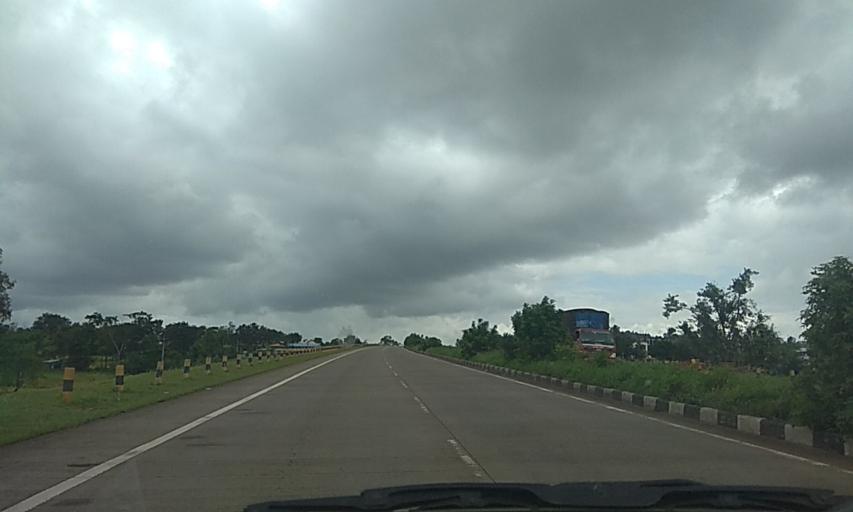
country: IN
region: Karnataka
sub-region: Belgaum
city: Sankeshwar
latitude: 16.2537
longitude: 74.4721
